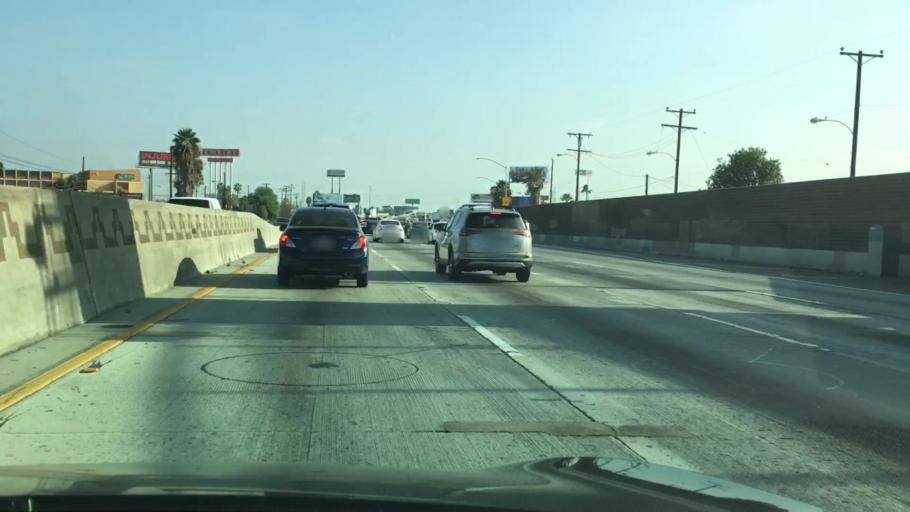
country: US
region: California
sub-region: Los Angeles County
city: Bell Gardens
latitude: 33.9788
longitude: -118.1279
